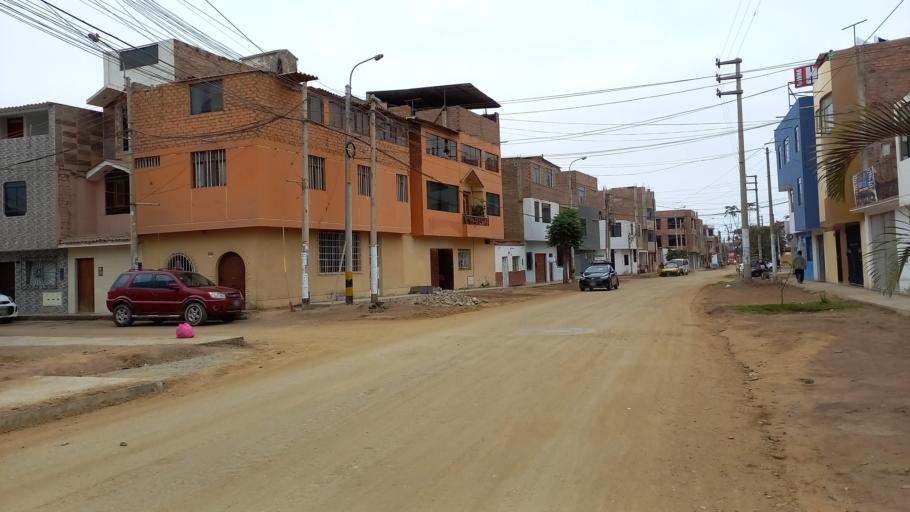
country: PE
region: La Libertad
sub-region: Provincia de Trujillo
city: Trujillo
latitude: -8.1027
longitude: -79.0436
